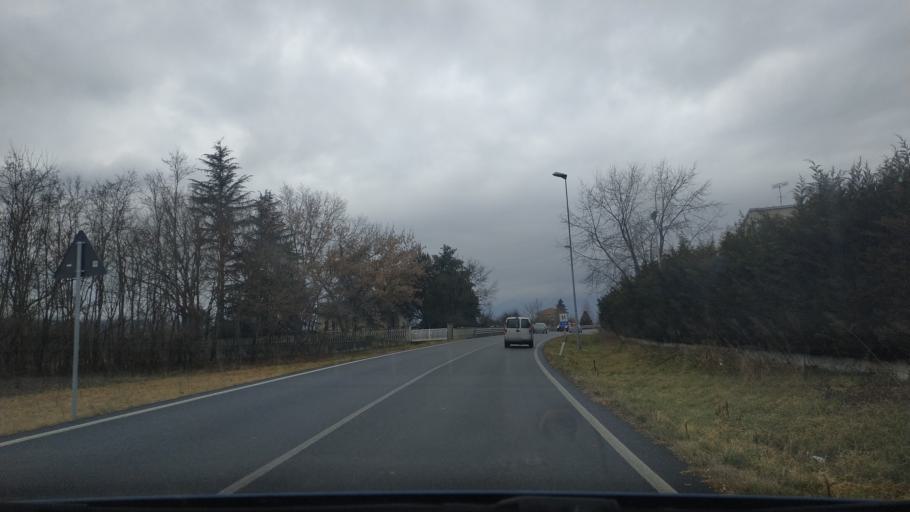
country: IT
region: Piedmont
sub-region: Provincia di Torino
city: Mercenasco
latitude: 45.3645
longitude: 7.8770
